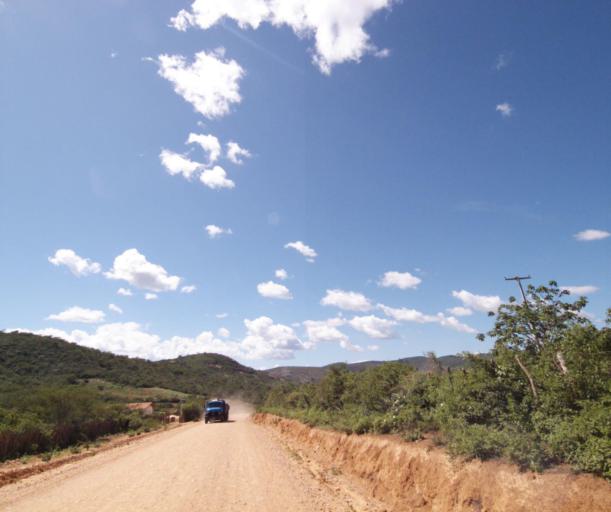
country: BR
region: Bahia
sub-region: Pocoes
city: Pocoes
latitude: -14.2675
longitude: -40.6964
